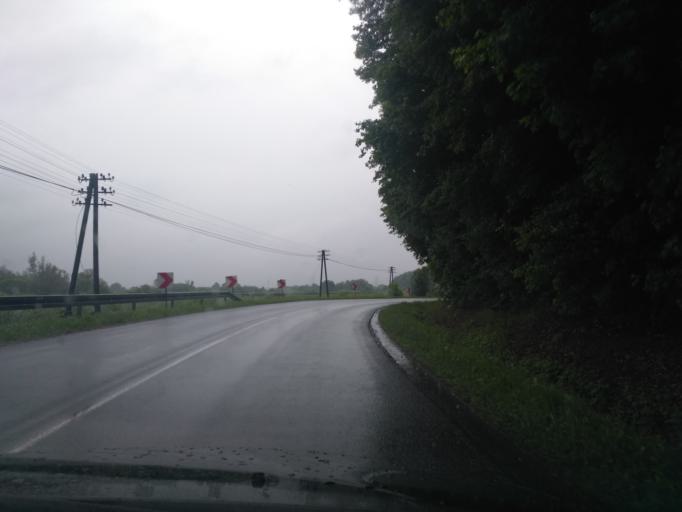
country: PL
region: Subcarpathian Voivodeship
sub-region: Powiat krosnienski
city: Leki
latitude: 49.8185
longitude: 21.6341
